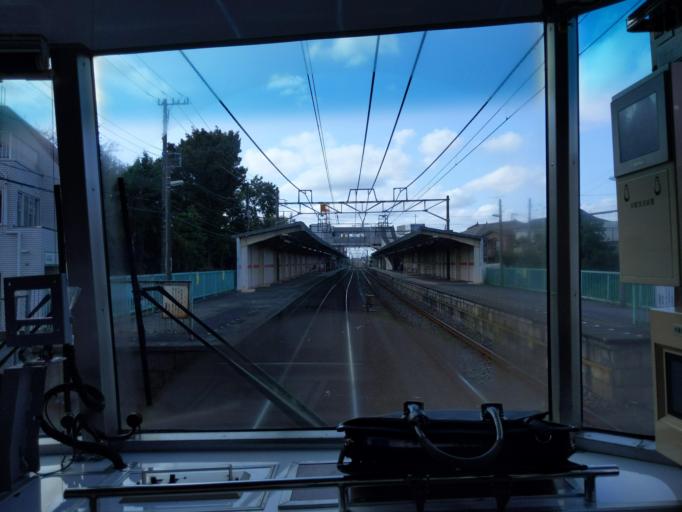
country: JP
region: Chiba
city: Shiroi
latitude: 35.7534
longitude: 140.0250
